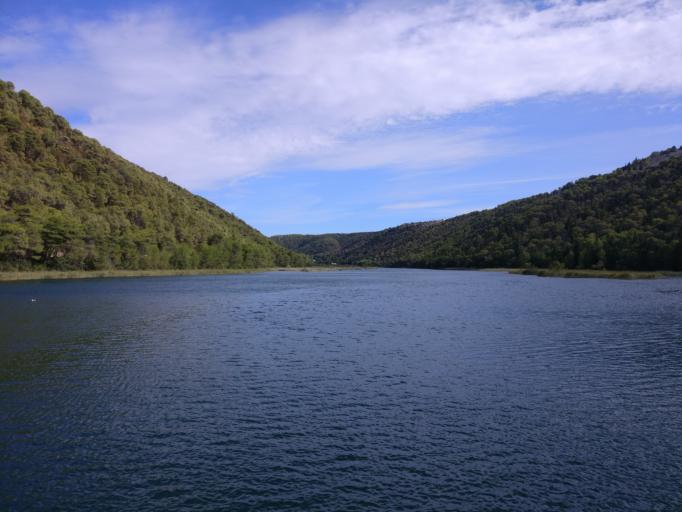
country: HR
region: Sibensko-Kniniska
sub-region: Grad Sibenik
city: Sibenik
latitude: 43.8201
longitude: 15.9475
